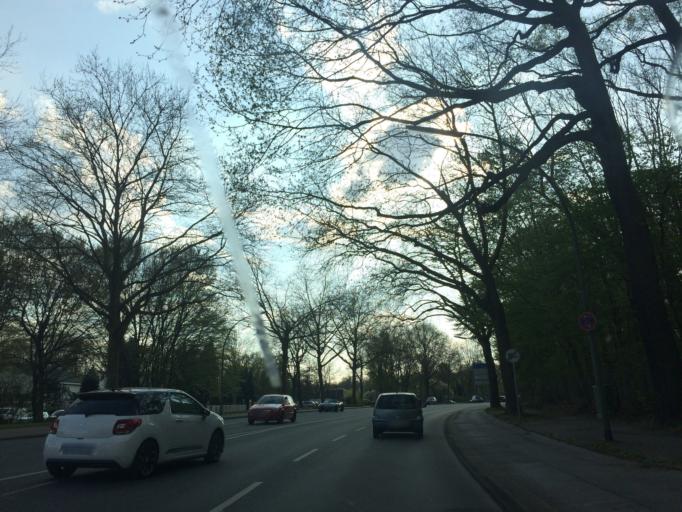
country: DE
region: North Rhine-Westphalia
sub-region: Regierungsbezirk Munster
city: Gelsenkirchen
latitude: 51.5656
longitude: 7.0731
